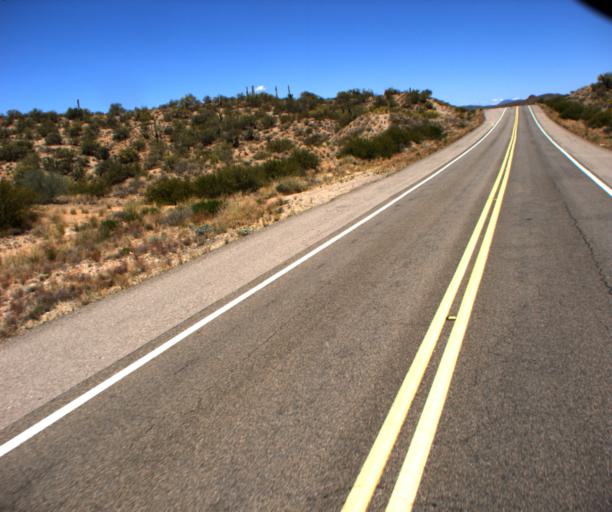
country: US
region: Arizona
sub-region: Yavapai County
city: Bagdad
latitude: 34.4307
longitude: -113.2442
